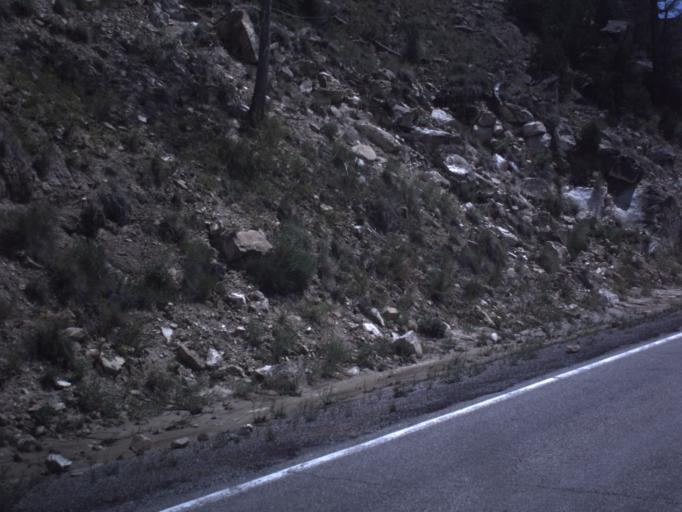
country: US
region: Utah
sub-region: Emery County
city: Orangeville
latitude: 39.2927
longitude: -111.2716
